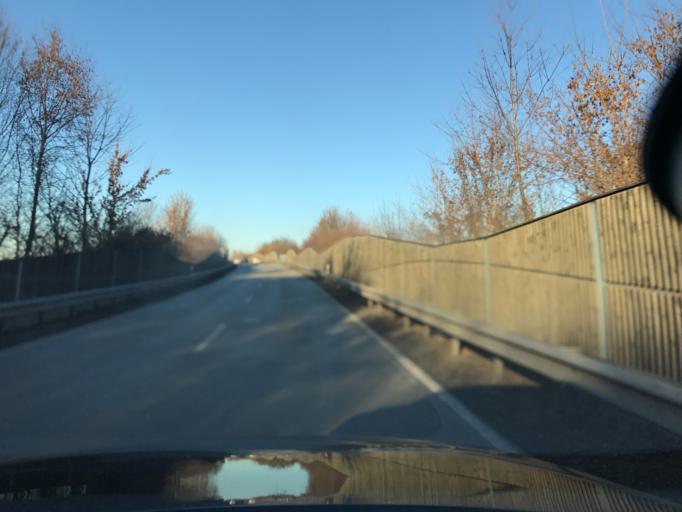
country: DE
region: Bavaria
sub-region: Upper Bavaria
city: Bad Aibling
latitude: 47.8640
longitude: 11.9878
